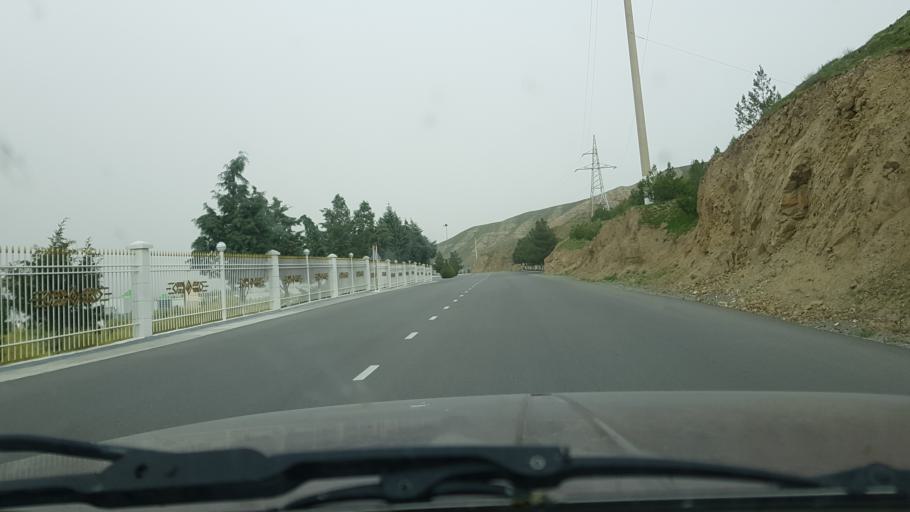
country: TM
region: Ahal
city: Arcabil
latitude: 38.0407
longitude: 58.0150
